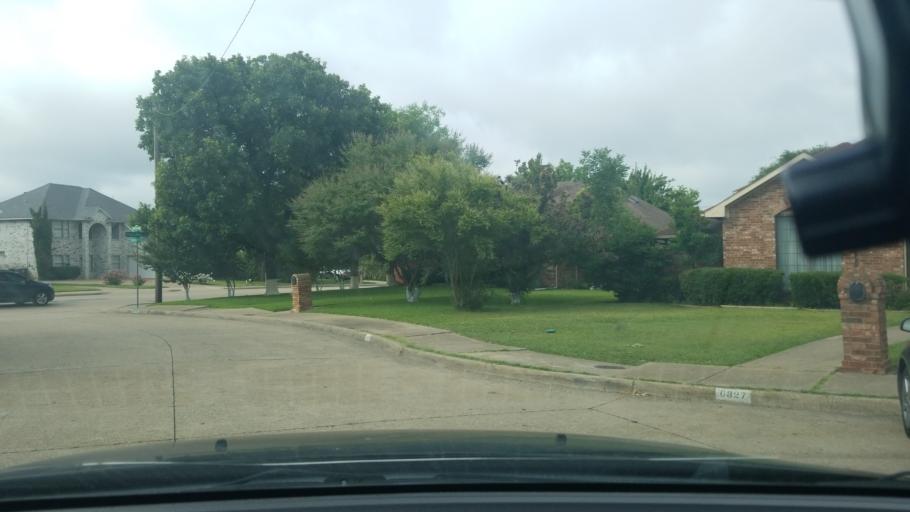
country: US
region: Texas
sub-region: Dallas County
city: Balch Springs
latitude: 32.7871
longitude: -96.6934
